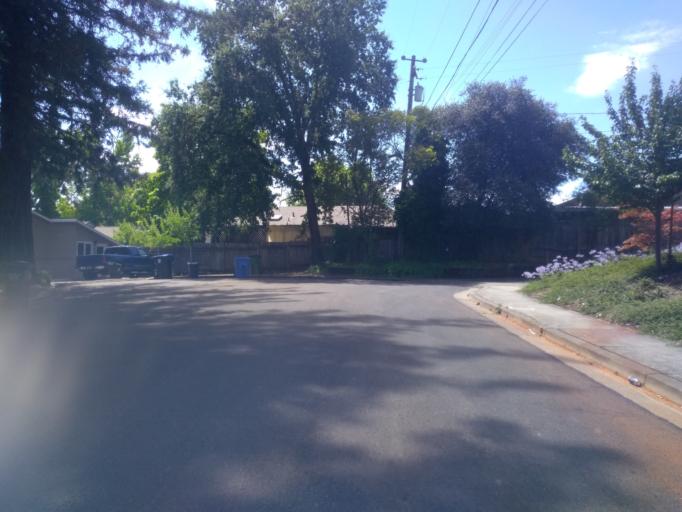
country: US
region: California
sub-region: Mendocino County
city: Ukiah
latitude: 39.1452
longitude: -123.2176
